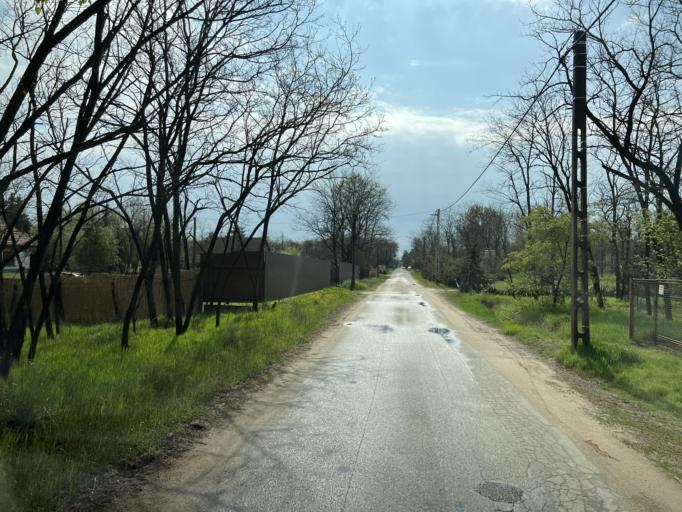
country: HU
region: Pest
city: Hernad
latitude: 47.1805
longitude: 19.4606
